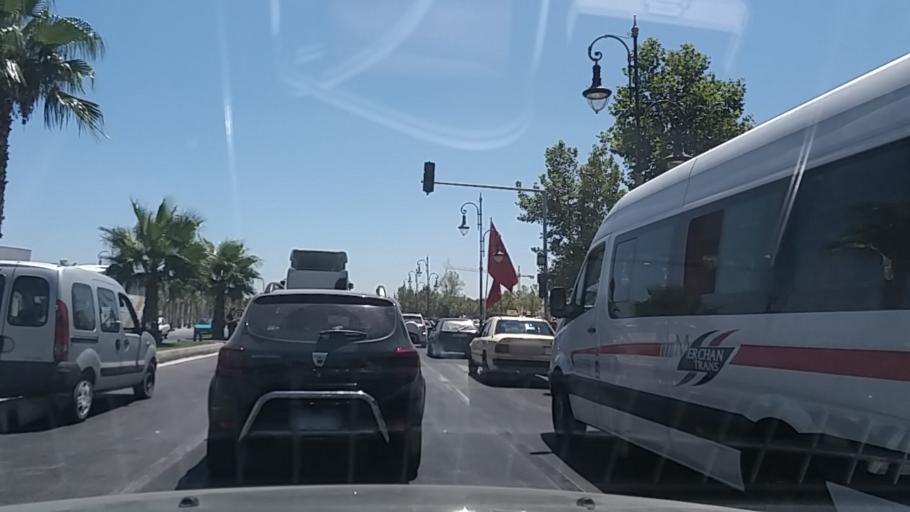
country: MA
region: Tanger-Tetouan
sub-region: Tanger-Assilah
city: Tangier
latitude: 35.7574
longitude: -5.7923
